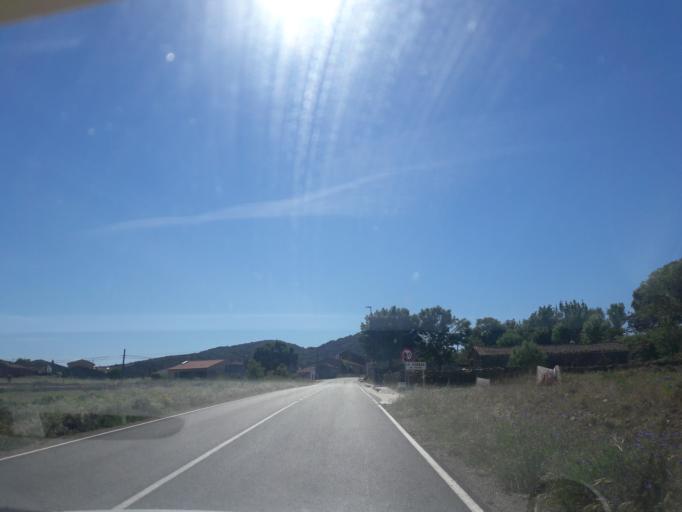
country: ES
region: Castille and Leon
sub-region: Provincia de Salamanca
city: Nava de Bejar
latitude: 40.4957
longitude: -5.6667
